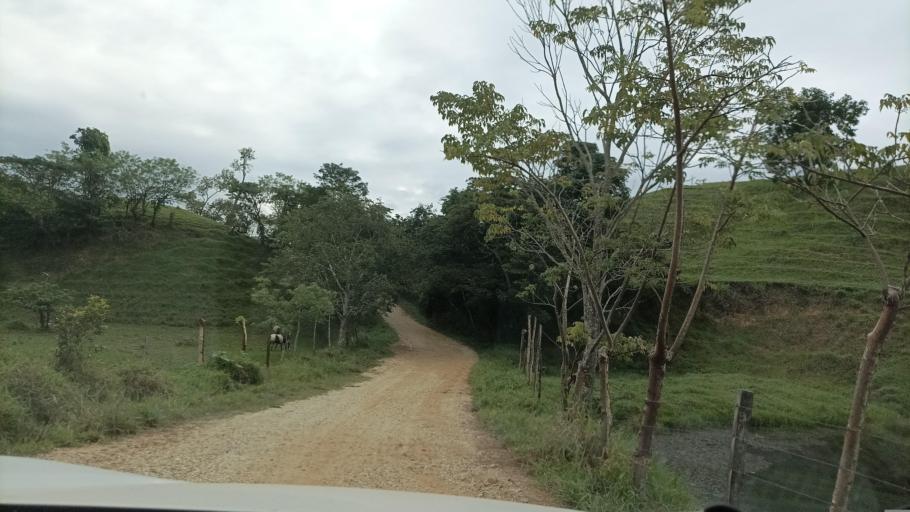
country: MX
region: Veracruz
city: Hidalgotitlan
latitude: 17.5987
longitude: -94.4228
